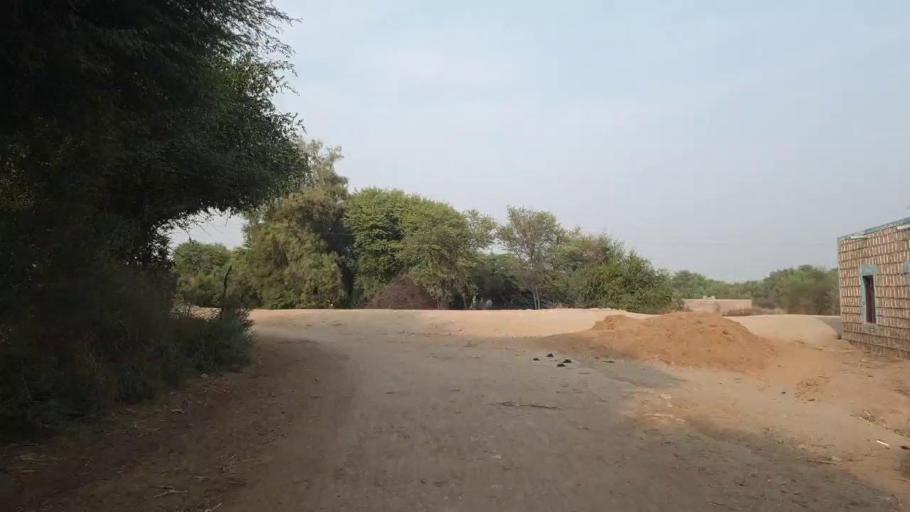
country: PK
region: Sindh
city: Sann
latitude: 26.1268
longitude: 68.0642
